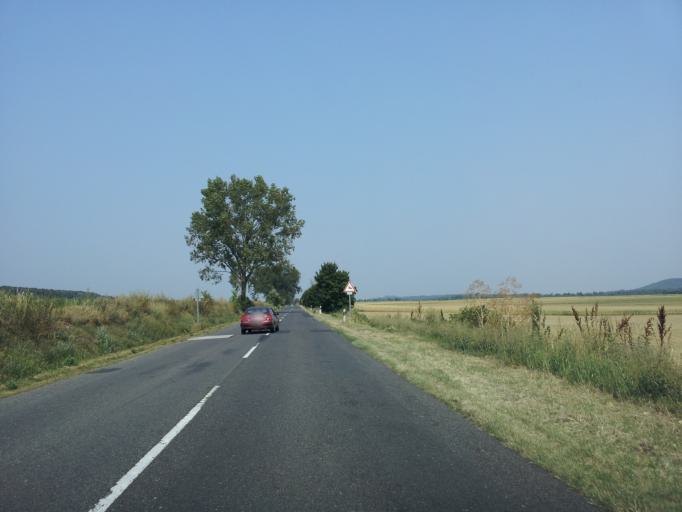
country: HU
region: Gyor-Moson-Sopron
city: Pannonhalma
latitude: 47.4739
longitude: 17.7926
